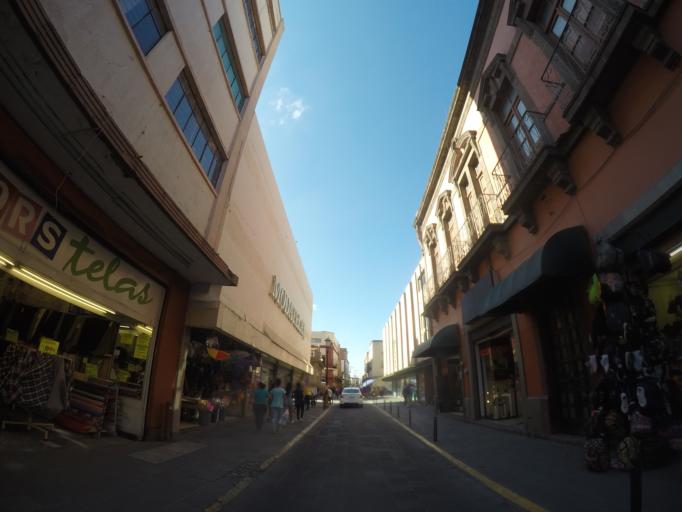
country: MX
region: San Luis Potosi
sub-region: San Luis Potosi
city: San Luis Potosi
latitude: 22.1537
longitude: -100.9750
